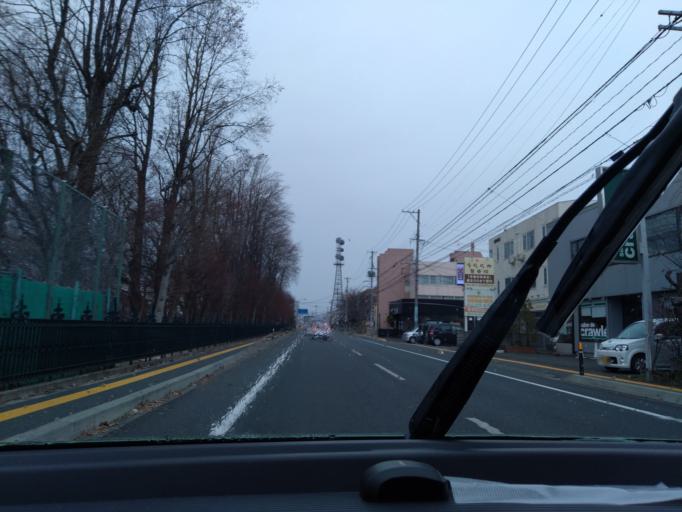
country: JP
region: Iwate
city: Morioka-shi
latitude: 39.7174
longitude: 141.1383
